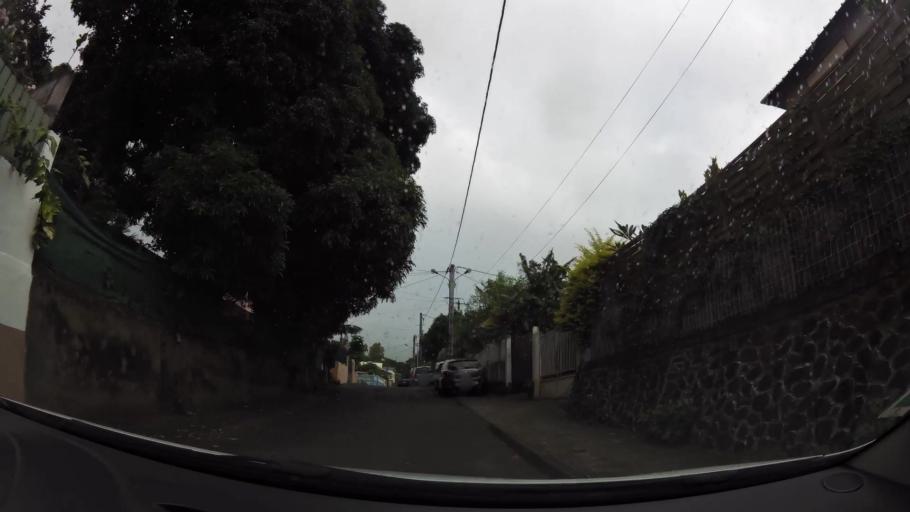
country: RE
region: Reunion
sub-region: Reunion
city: Sainte-Marie
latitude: -20.8998
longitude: 55.5481
